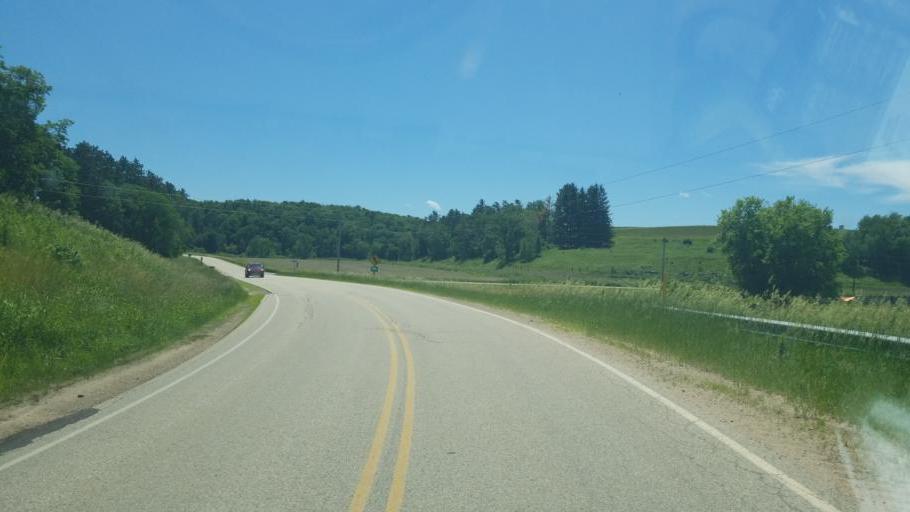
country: US
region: Wisconsin
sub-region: Juneau County
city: Elroy
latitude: 43.7961
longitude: -90.3024
